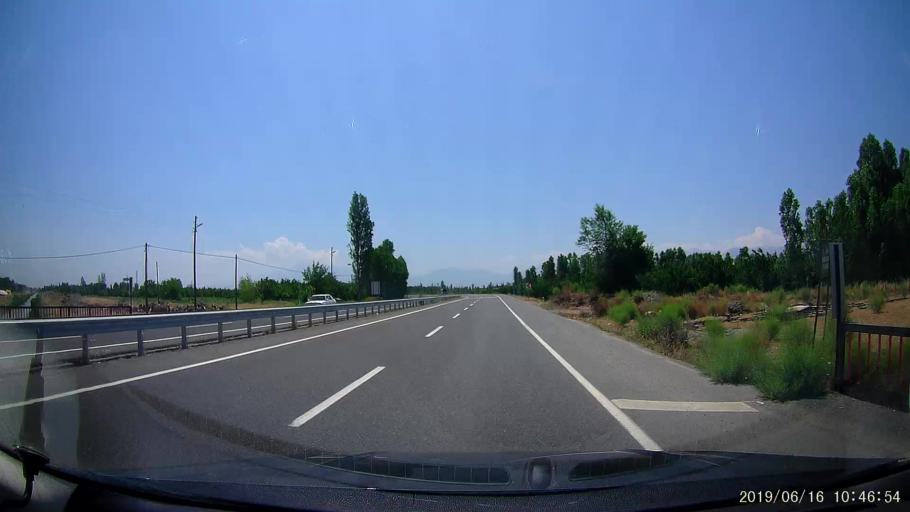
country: AM
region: Armavir
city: Shenavan
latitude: 40.0170
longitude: 43.8824
